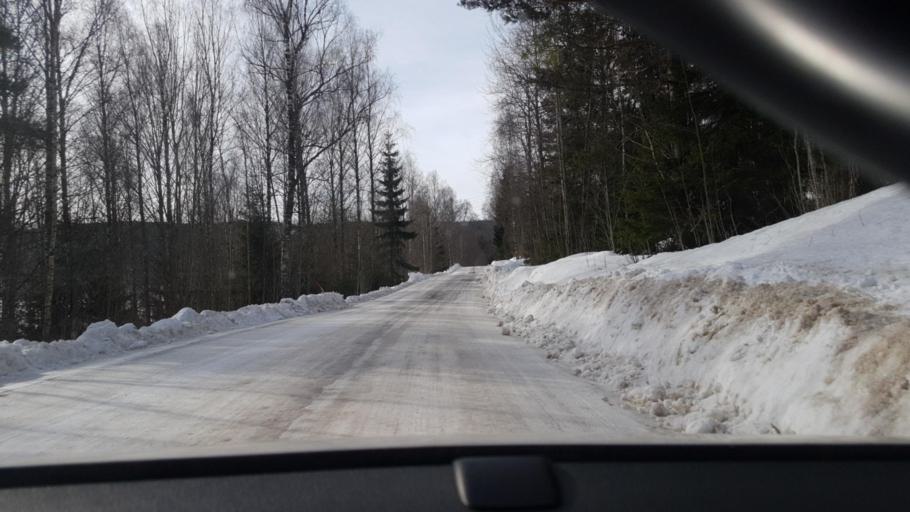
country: NO
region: Ostfold
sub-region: Romskog
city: Romskog
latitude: 59.8351
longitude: 11.9591
